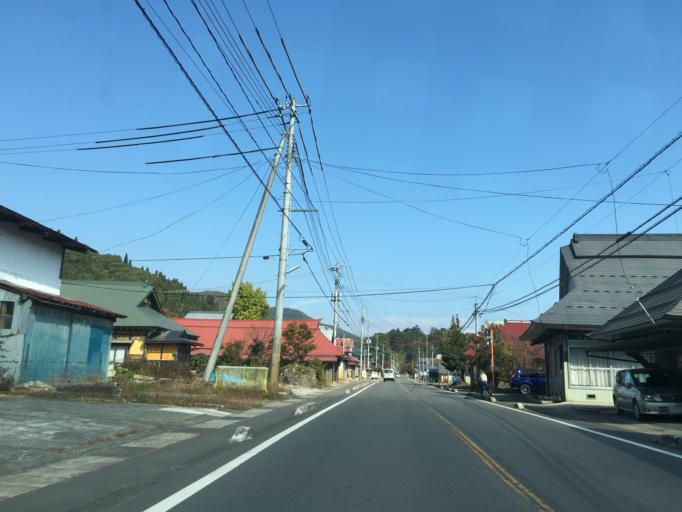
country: JP
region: Fukushima
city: Inawashiro
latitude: 37.4022
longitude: 140.0683
